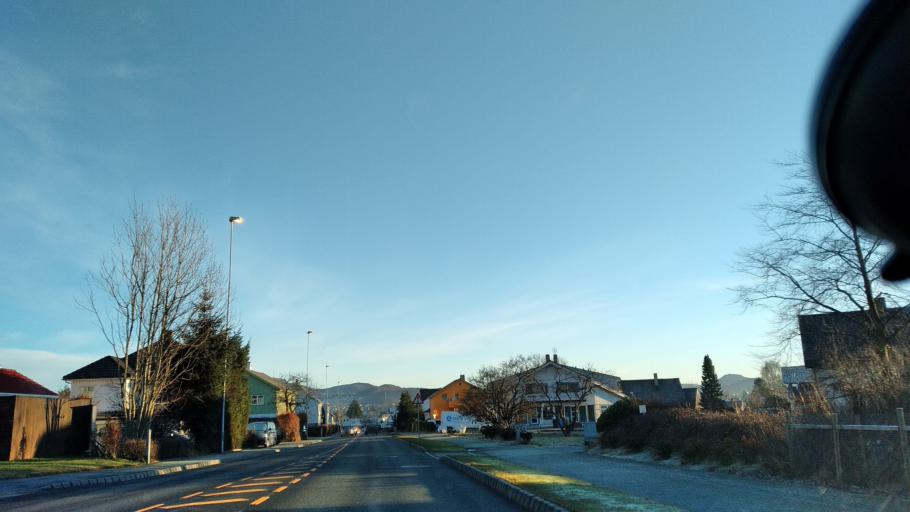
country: NO
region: Rogaland
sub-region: Sandnes
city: Sandnes
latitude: 58.8543
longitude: 5.7174
